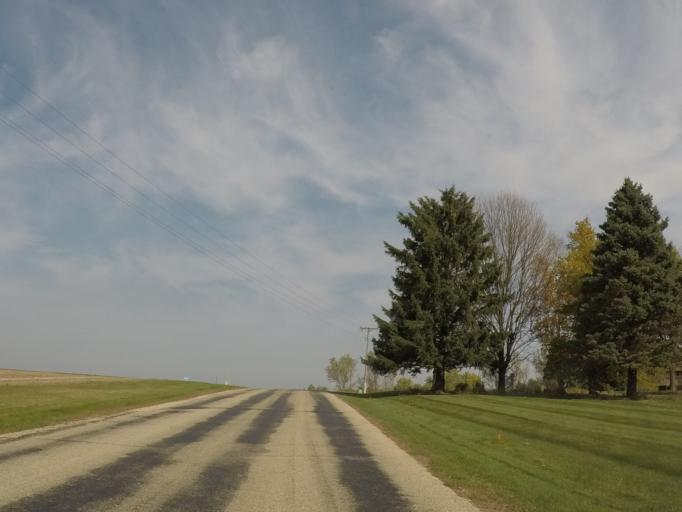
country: US
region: Wisconsin
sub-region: Dane County
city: Cross Plains
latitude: 43.0510
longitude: -89.6010
